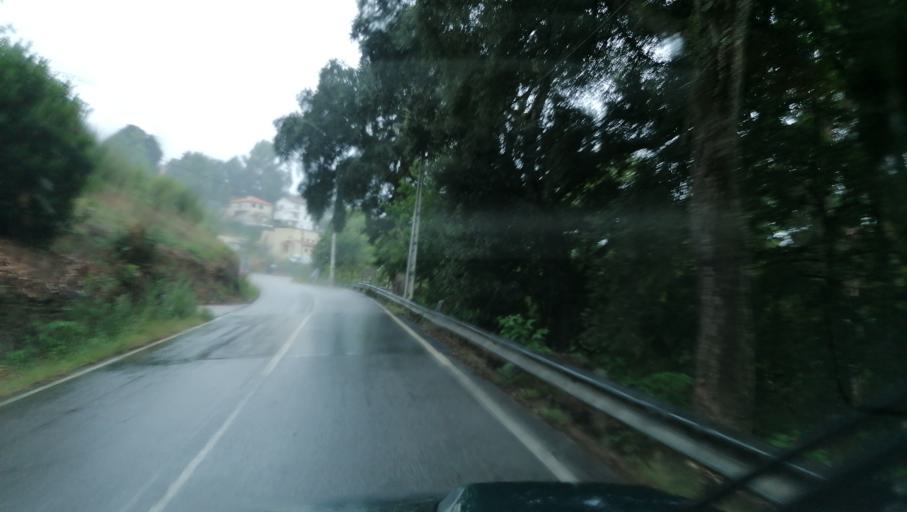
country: PT
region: Braga
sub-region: Cabeceiras de Basto
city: Cabeceiras de Basto
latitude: 41.4914
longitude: -7.9591
